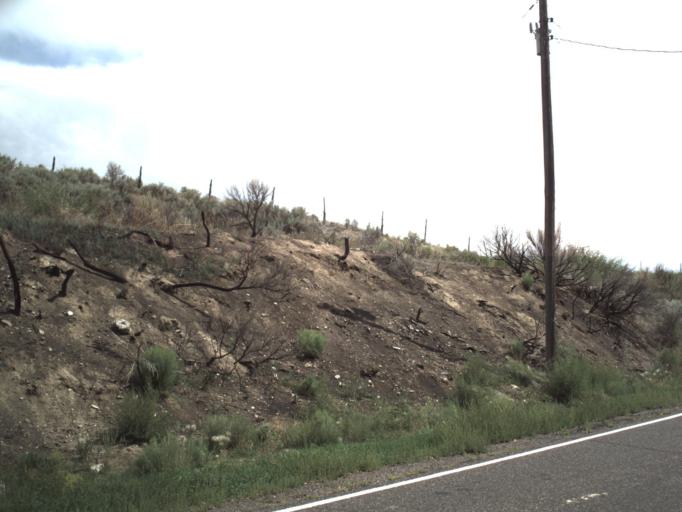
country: US
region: Utah
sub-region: Piute County
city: Junction
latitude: 38.1259
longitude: -112.0004
